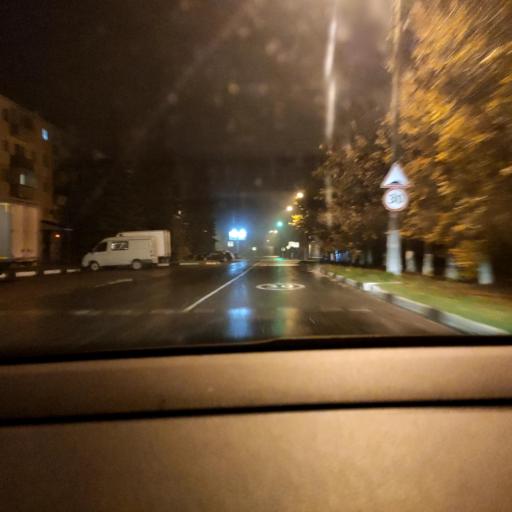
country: RU
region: Moskovskaya
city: Ivanteyevka
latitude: 55.9659
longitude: 37.9072
